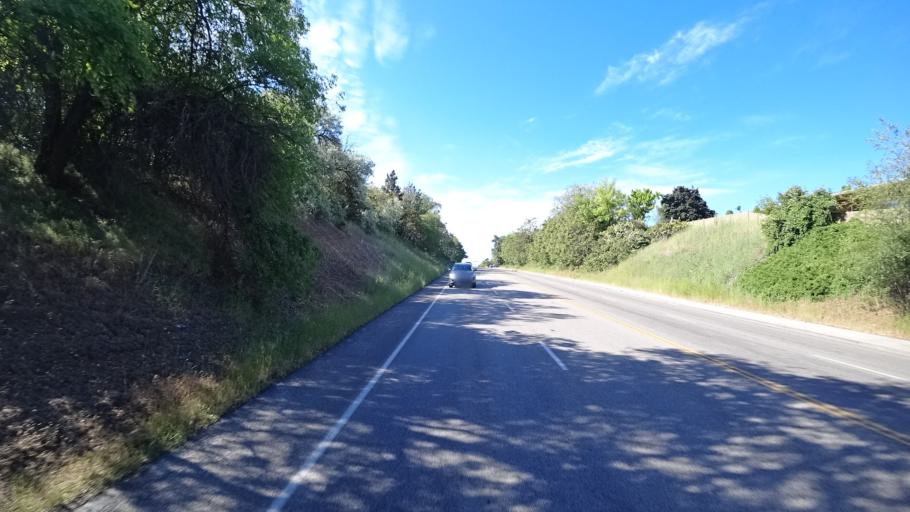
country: US
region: Idaho
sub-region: Ada County
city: Garden City
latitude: 43.5882
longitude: -116.2436
